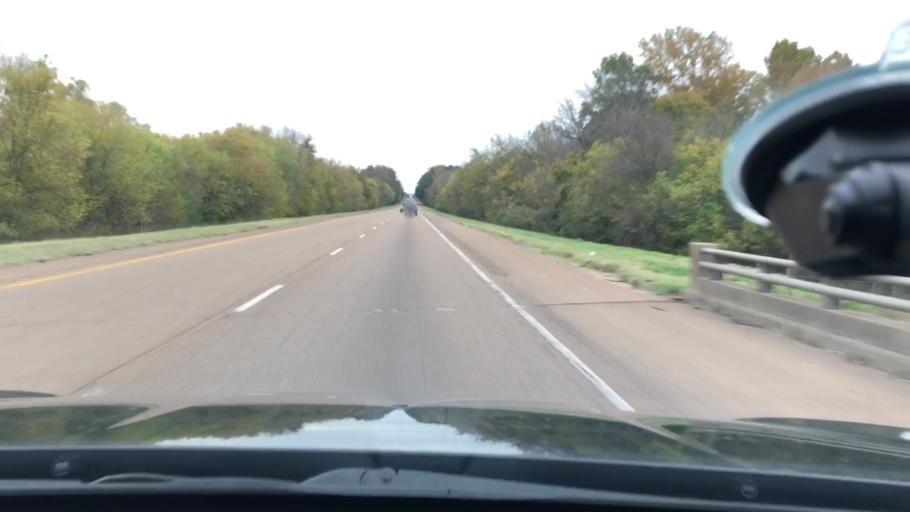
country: US
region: Arkansas
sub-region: Nevada County
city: Prescott
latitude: 33.7581
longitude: -93.4950
